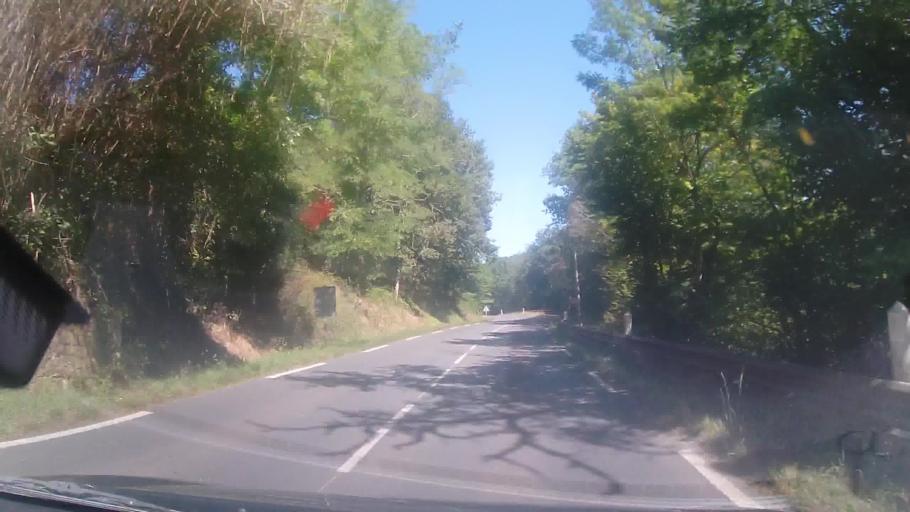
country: FR
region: Aquitaine
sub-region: Departement de la Dordogne
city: Carsac-Aillac
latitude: 44.8488
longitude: 1.2144
